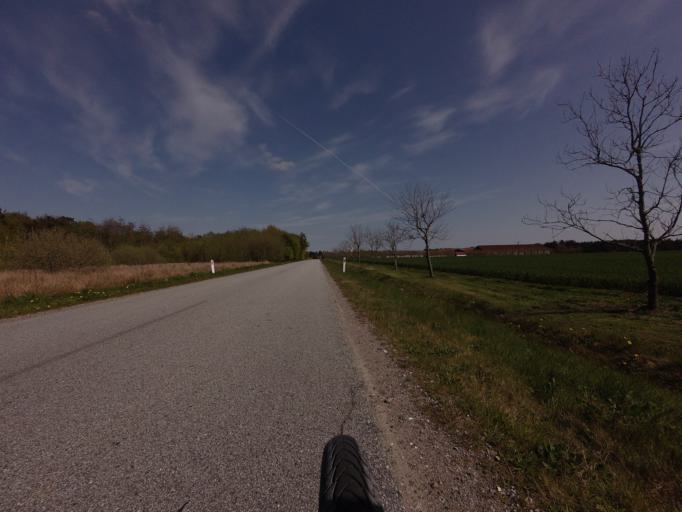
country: DK
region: North Denmark
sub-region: Jammerbugt Kommune
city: Pandrup
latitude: 57.2285
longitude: 9.6228
